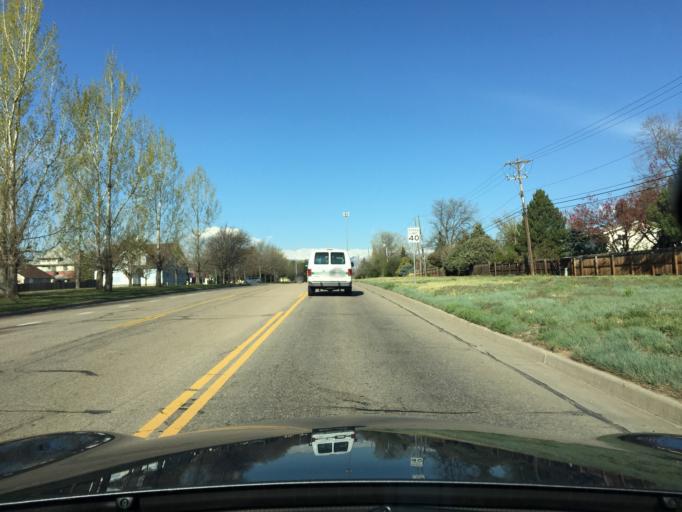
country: US
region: Colorado
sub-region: Boulder County
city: Longmont
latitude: 40.1382
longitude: -105.1033
